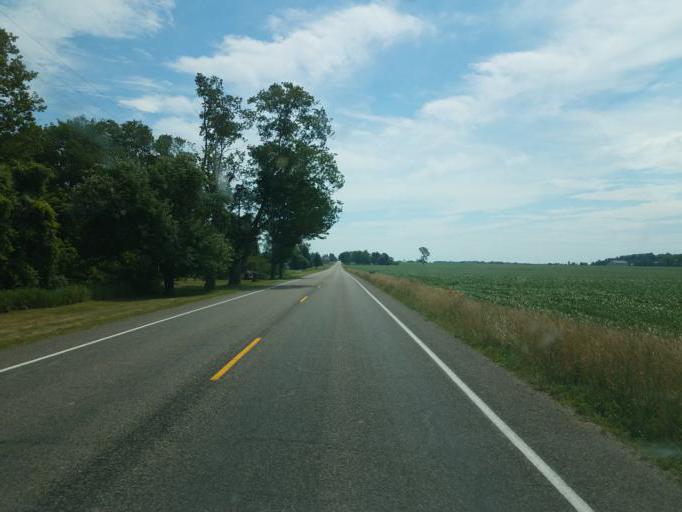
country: US
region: Michigan
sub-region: Eaton County
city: Charlotte
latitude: 42.6260
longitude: -84.8270
